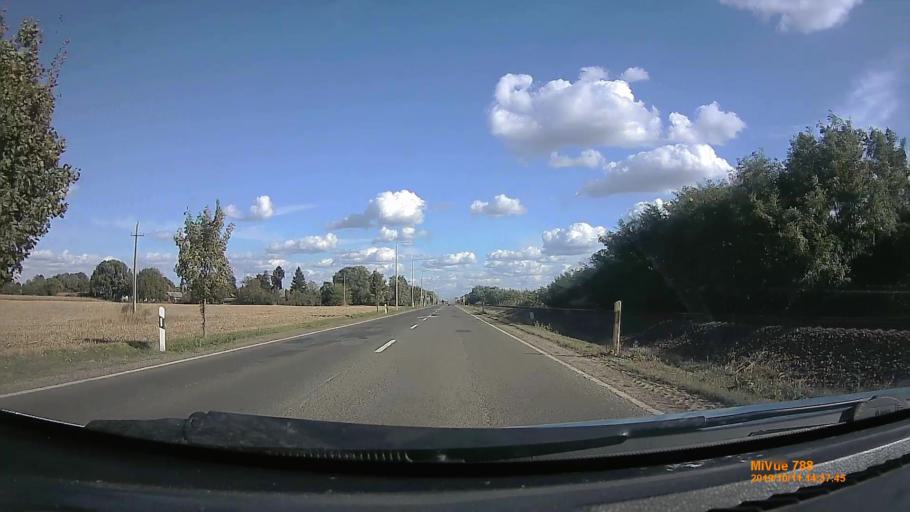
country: HU
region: Hajdu-Bihar
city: Ebes
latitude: 47.5531
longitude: 21.5315
